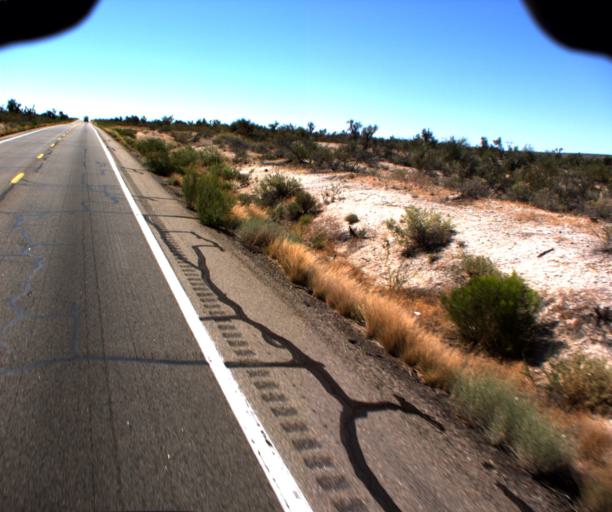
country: US
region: Arizona
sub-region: Yavapai County
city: Bagdad
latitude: 34.2954
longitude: -113.1144
